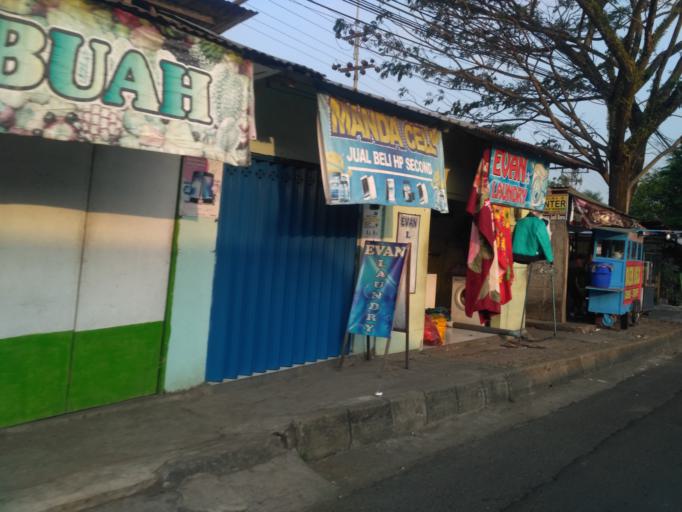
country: ID
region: East Java
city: Kepuh
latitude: -8.0023
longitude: 112.6178
